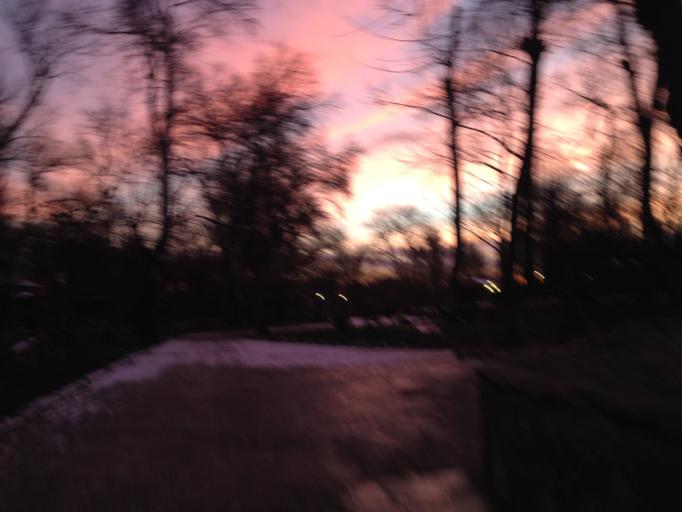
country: RU
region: Rostov
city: Staraya Stanitsa
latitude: 48.3525
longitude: 40.2963
